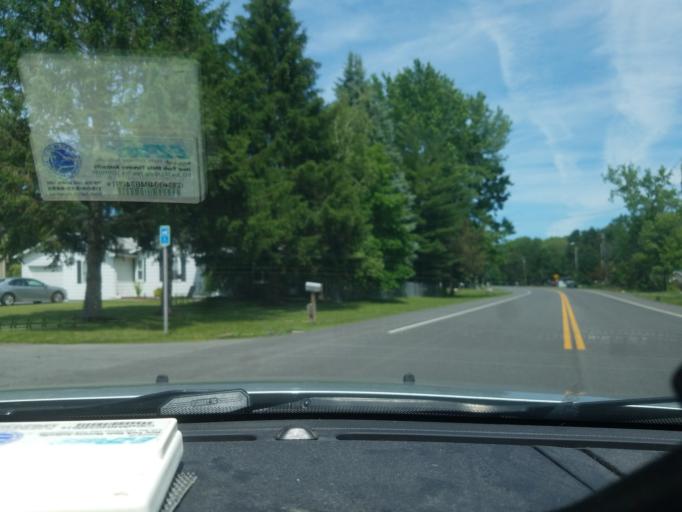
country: US
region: New York
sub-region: Onondaga County
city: East Syracuse
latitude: 43.0757
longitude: -76.0682
